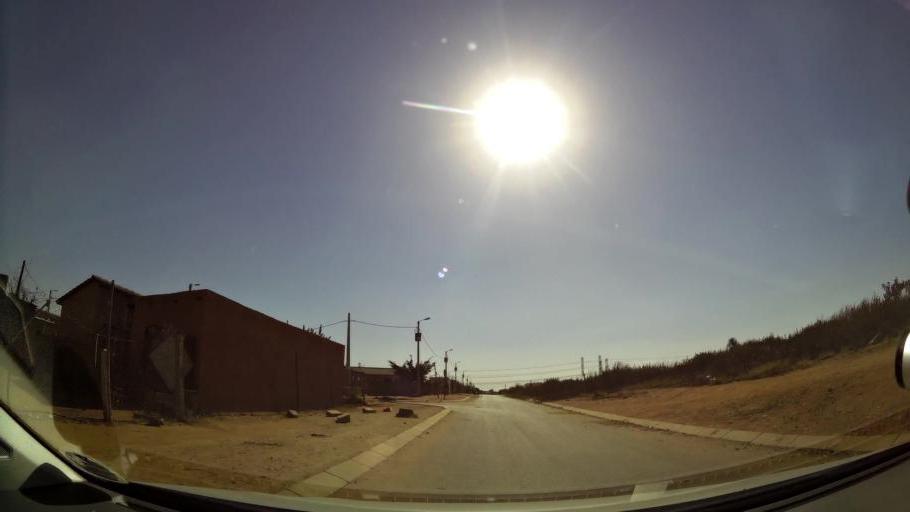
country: ZA
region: Gauteng
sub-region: Ekurhuleni Metropolitan Municipality
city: Tembisa
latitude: -26.0319
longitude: 28.2276
